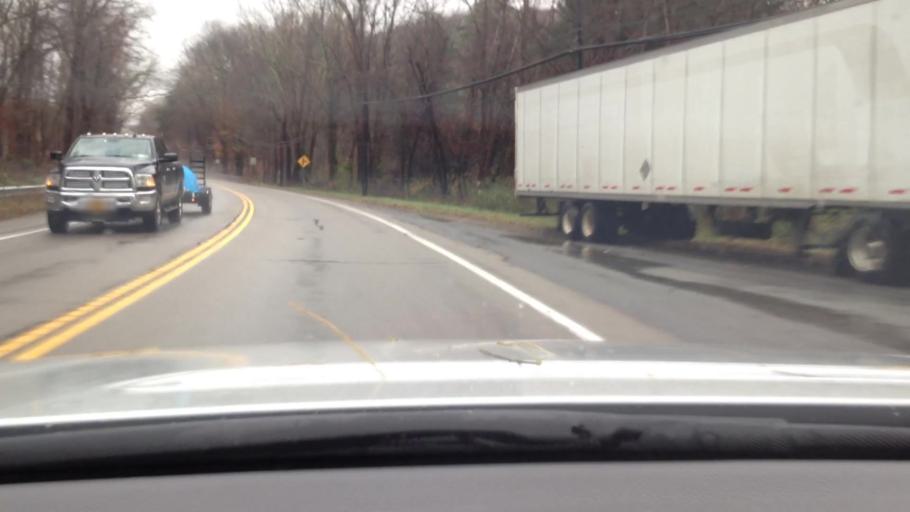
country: US
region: New York
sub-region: Westchester County
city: Peekskill
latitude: 41.3271
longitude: -73.9276
